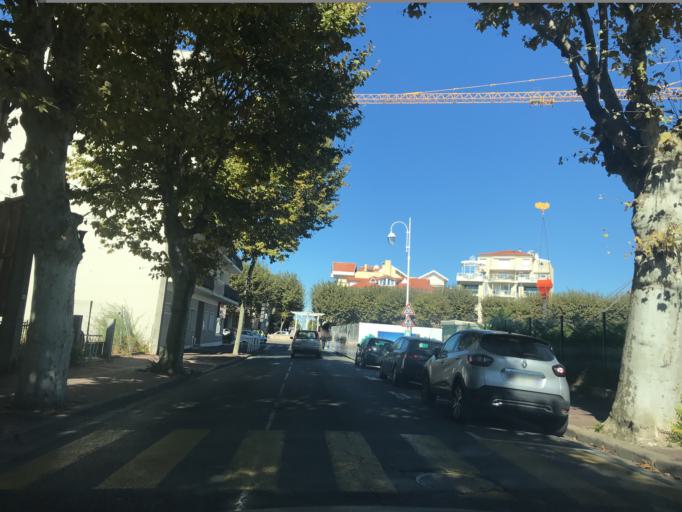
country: FR
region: Aquitaine
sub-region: Departement de la Gironde
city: Arcachon
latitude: 44.6588
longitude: -1.1682
